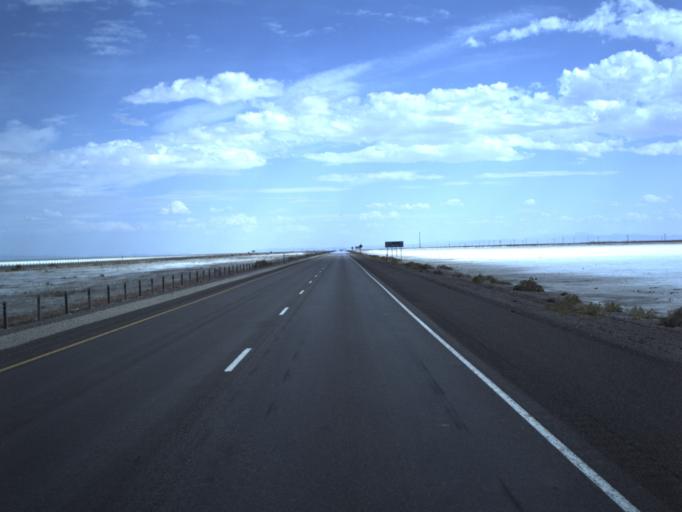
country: US
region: Utah
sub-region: Tooele County
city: Wendover
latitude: 40.7383
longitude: -113.8422
